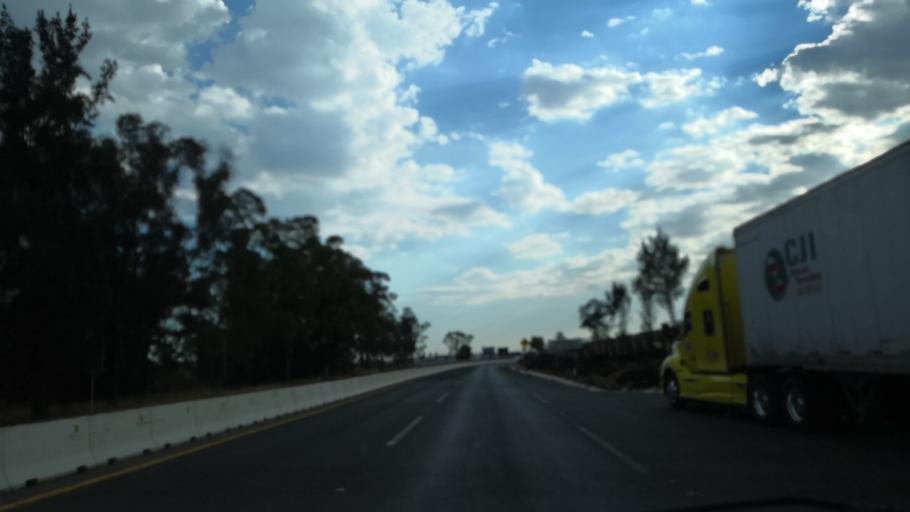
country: MX
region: Guanajuato
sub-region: Guanajuato
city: San Jose de Cervera
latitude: 20.9810
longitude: -101.2912
